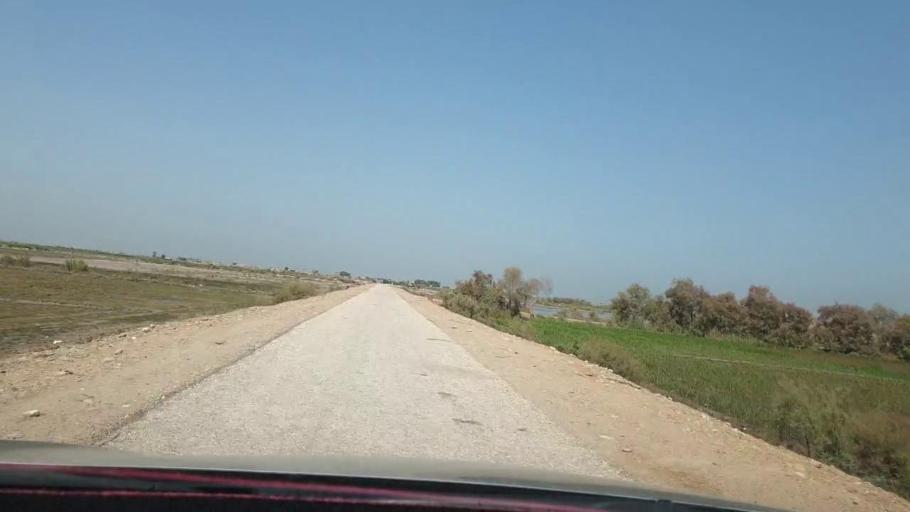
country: PK
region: Sindh
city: Warah
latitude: 27.5691
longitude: 67.7547
